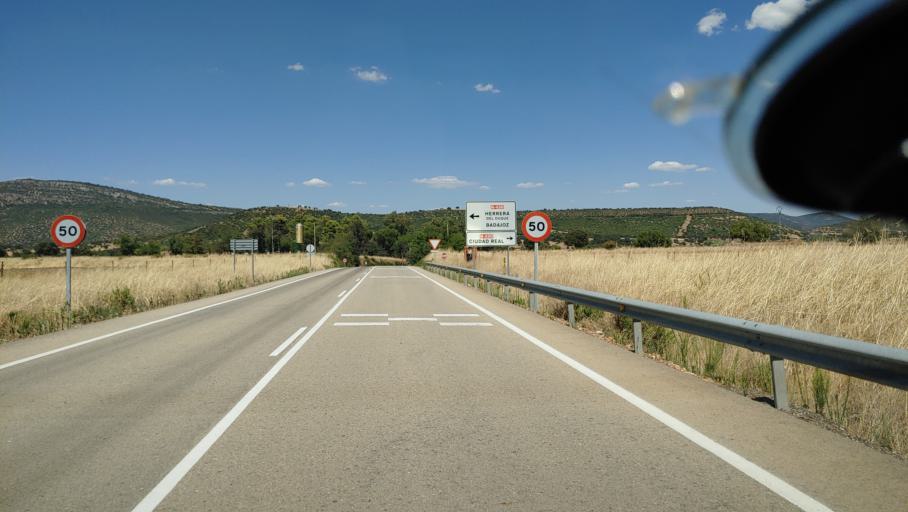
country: ES
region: Castille-La Mancha
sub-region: Provincia de Ciudad Real
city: Saceruela
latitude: 39.0143
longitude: -4.4953
